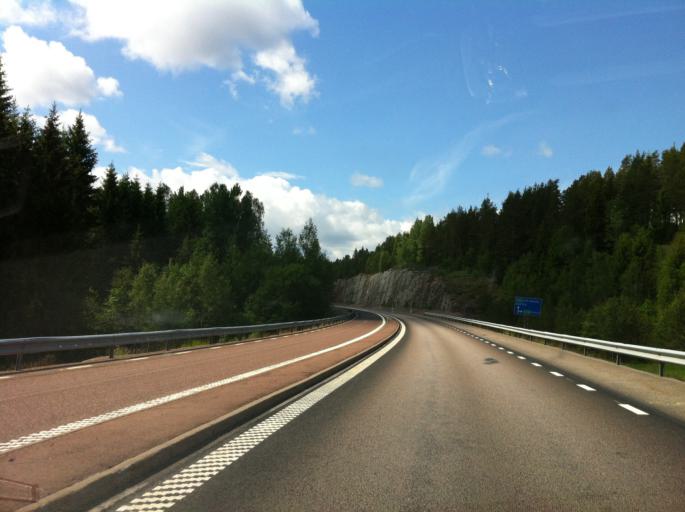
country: SE
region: Vaermland
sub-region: Grums Kommun
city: Slottsbron
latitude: 59.2625
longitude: 12.9986
